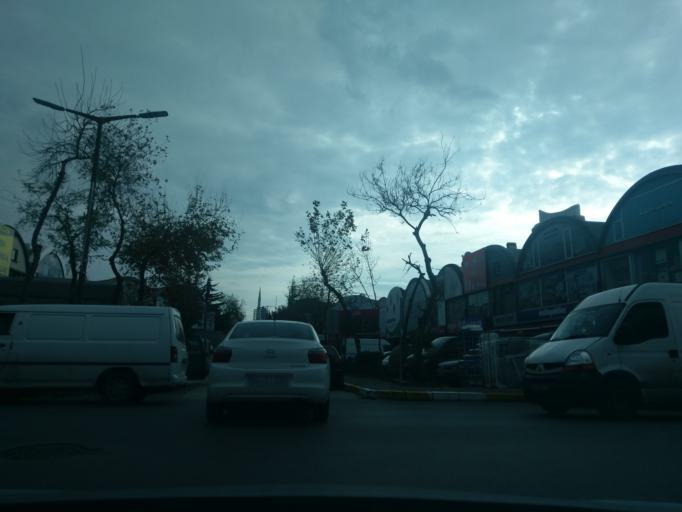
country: TR
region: Istanbul
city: Mahmutbey
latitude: 41.0683
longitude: 28.8234
